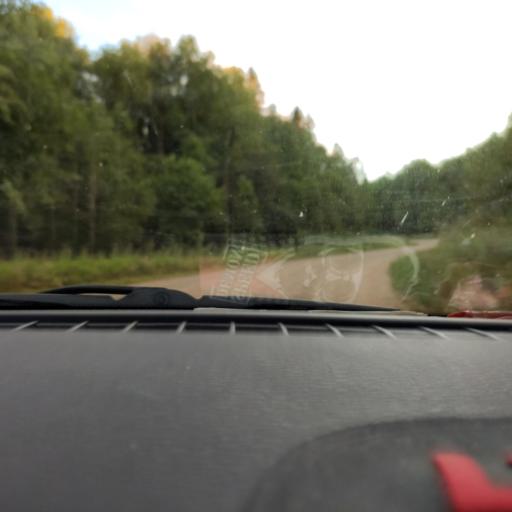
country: RU
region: Perm
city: Pavlovskiy
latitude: 57.9741
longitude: 54.8332
